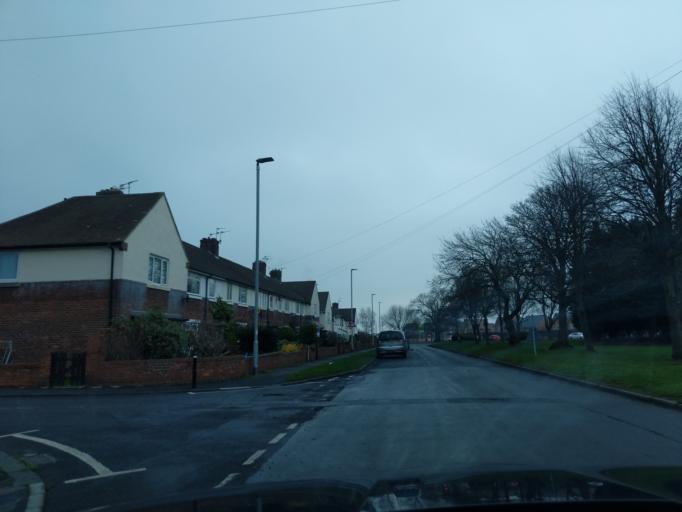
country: GB
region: England
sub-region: Northumberland
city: Morpeth
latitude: 55.1575
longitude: -1.6758
